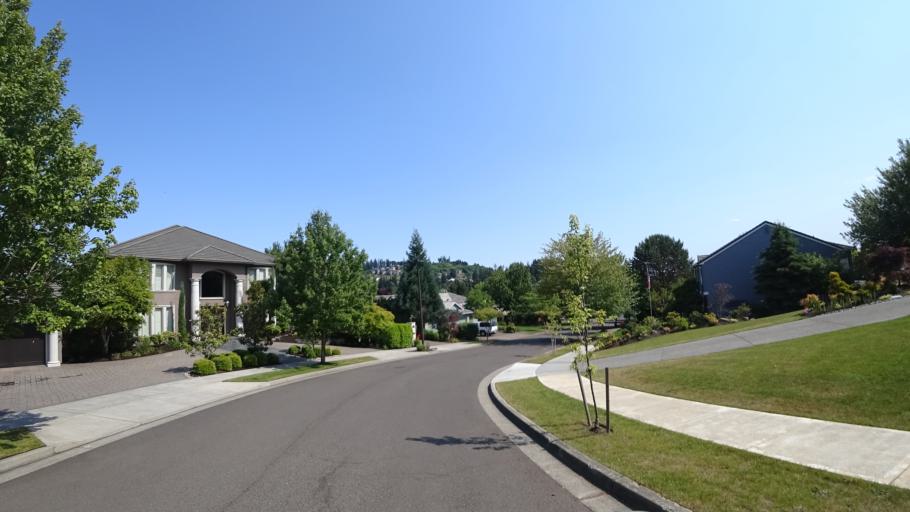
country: US
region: Oregon
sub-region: Clackamas County
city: Happy Valley
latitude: 45.4456
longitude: -122.5336
